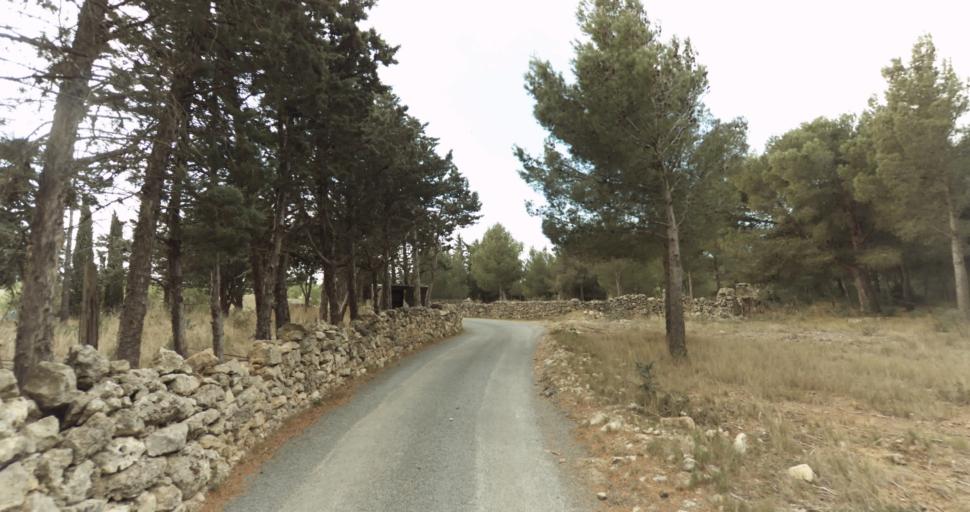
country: FR
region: Languedoc-Roussillon
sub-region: Departement de l'Aude
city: Leucate
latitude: 42.9316
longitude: 3.0239
